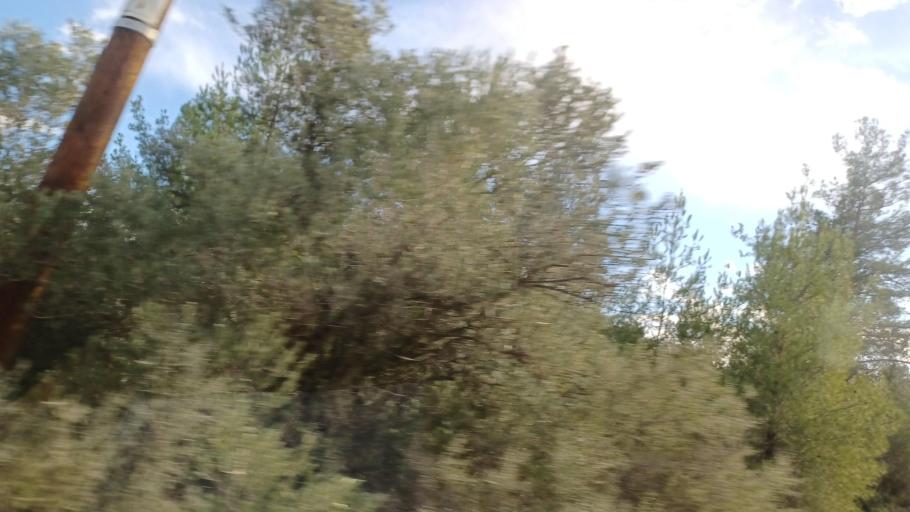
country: CY
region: Lefkosia
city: Lythrodontas
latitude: 34.9282
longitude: 33.2981
